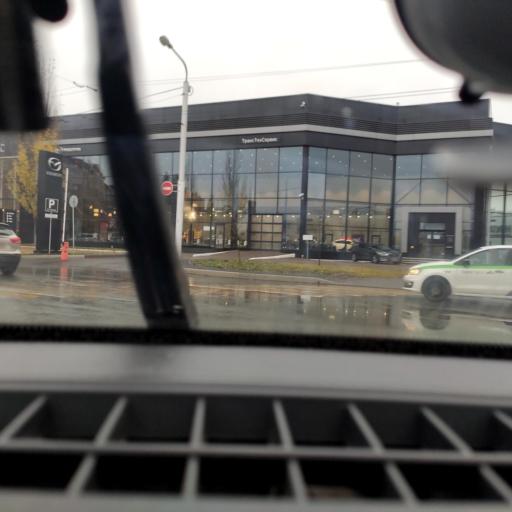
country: RU
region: Bashkortostan
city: Ufa
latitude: 54.7741
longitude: 56.0652
